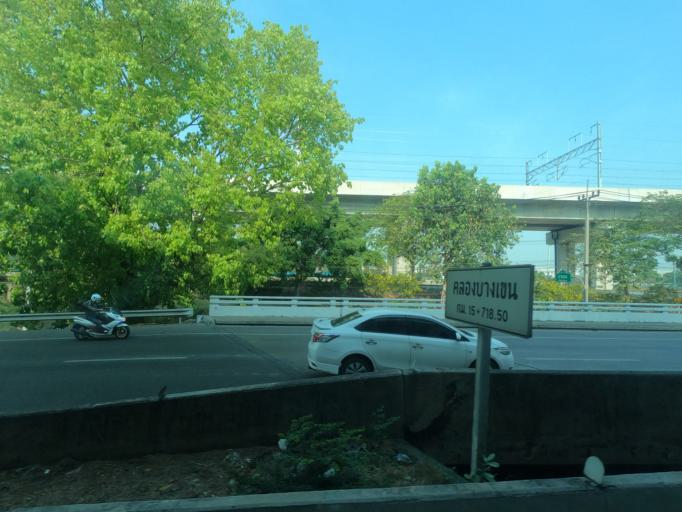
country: TH
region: Bangkok
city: Chatuchak
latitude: 13.8582
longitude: 100.5642
